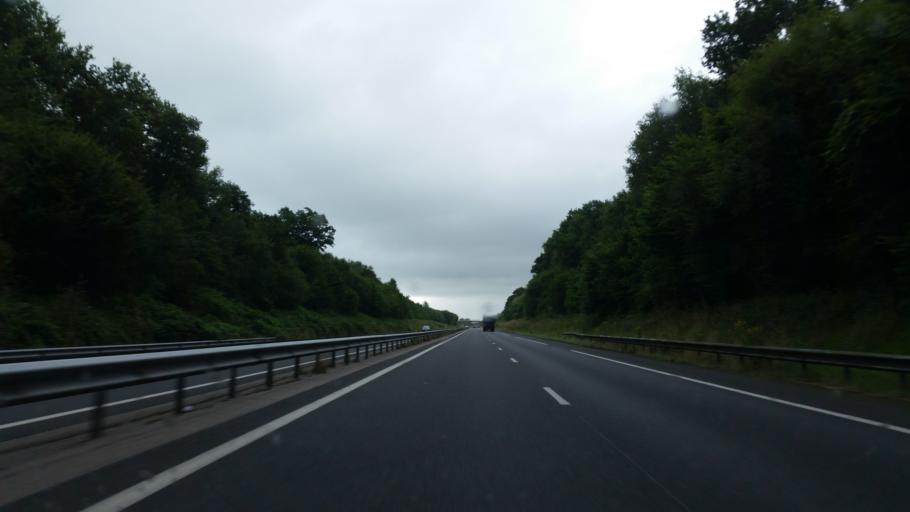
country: FR
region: Lower Normandy
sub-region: Departement du Calvados
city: Saint-Gatien-des-Bois
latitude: 49.3381
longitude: 0.2462
